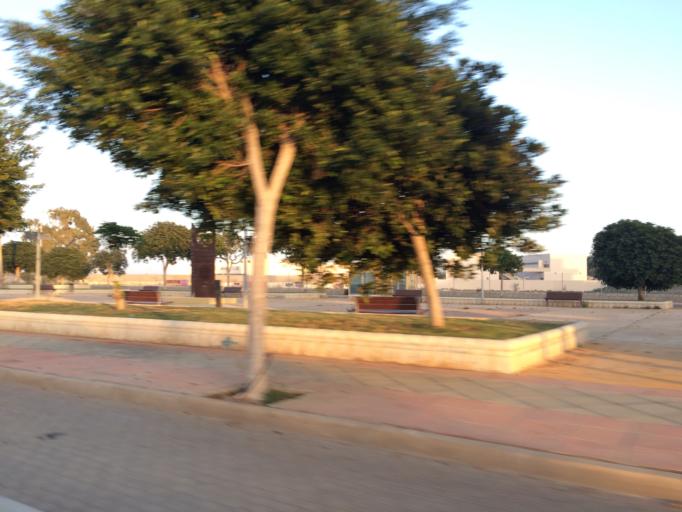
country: ES
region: Andalusia
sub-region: Provincia de Almeria
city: Almeria
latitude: 36.8253
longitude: -2.4393
